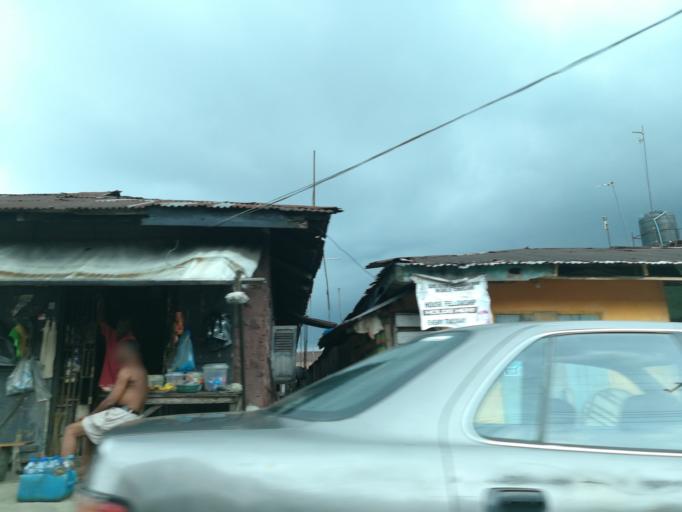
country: NG
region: Rivers
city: Port Harcourt
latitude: 4.7928
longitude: 6.9854
